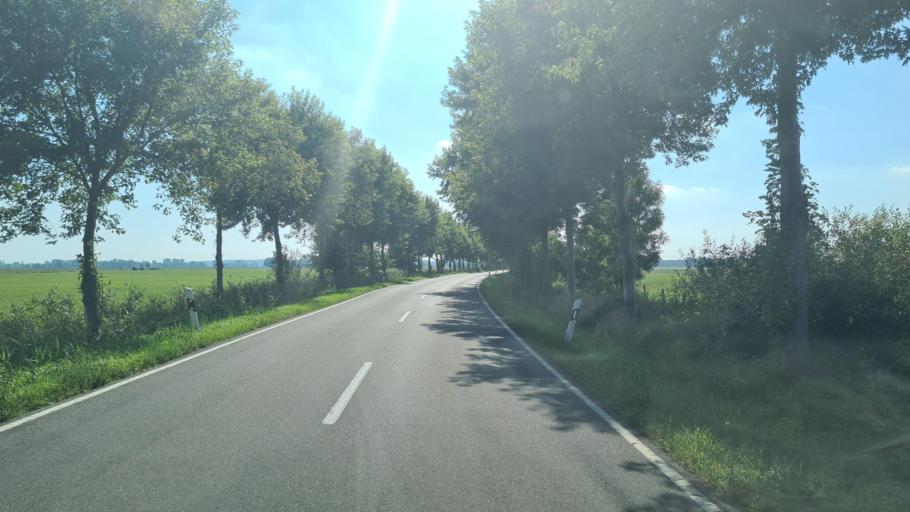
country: DE
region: Brandenburg
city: Friesack
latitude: 52.7760
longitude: 12.5944
